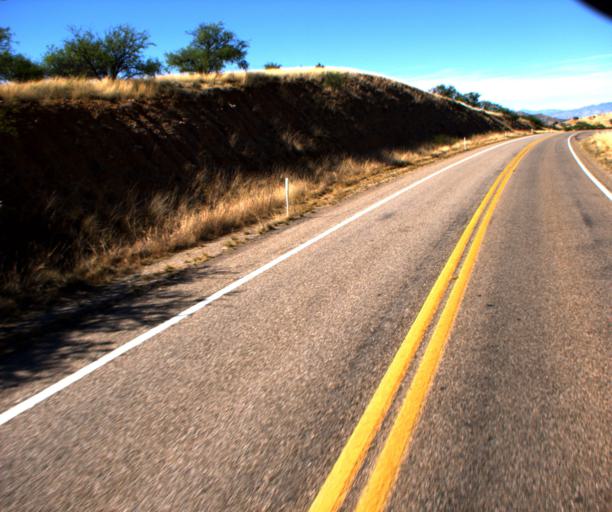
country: US
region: Arizona
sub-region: Pima County
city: Corona de Tucson
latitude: 31.8149
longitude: -110.7121
